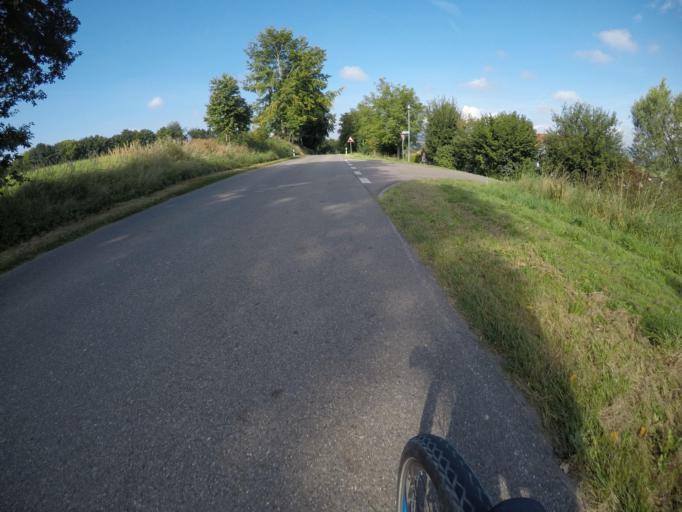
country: DE
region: Bavaria
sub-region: Swabia
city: Buttenwiesen
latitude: 48.6227
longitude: 10.7544
